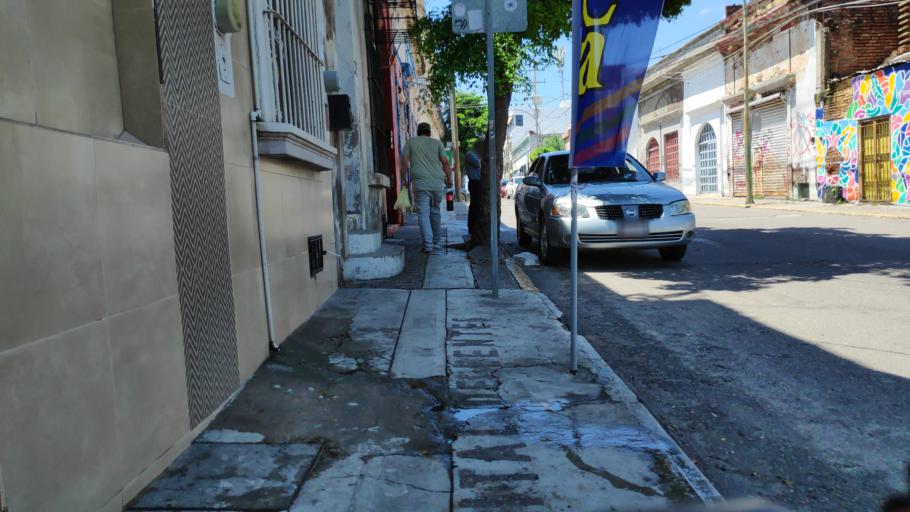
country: MX
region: Sinaloa
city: Culiacan
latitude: 24.8101
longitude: -107.3924
